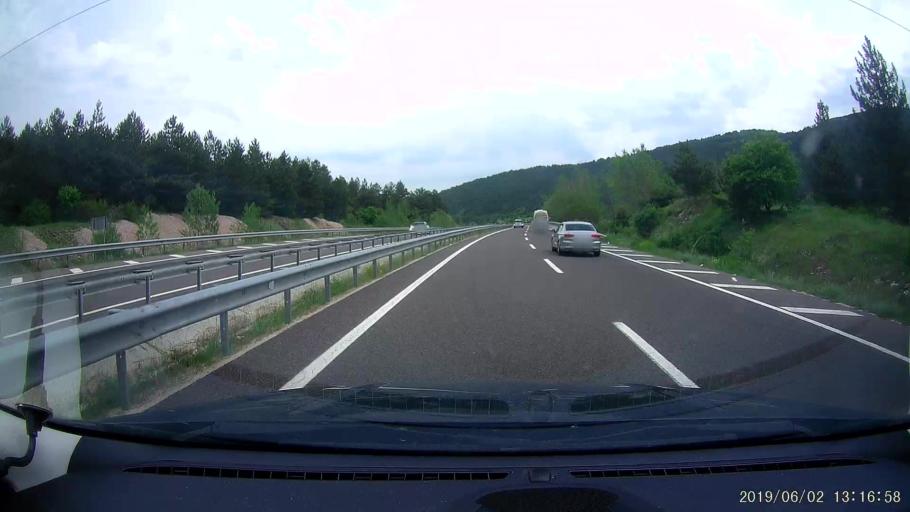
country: TR
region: Karabuk
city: Gozyeri
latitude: 40.8445
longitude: 32.6922
